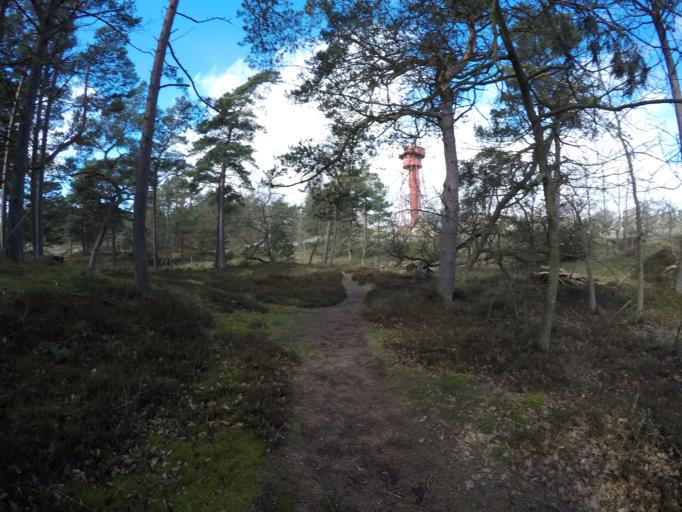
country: SE
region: Skane
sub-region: Simrishamns Kommun
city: Simrishamn
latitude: 55.3863
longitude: 14.1940
